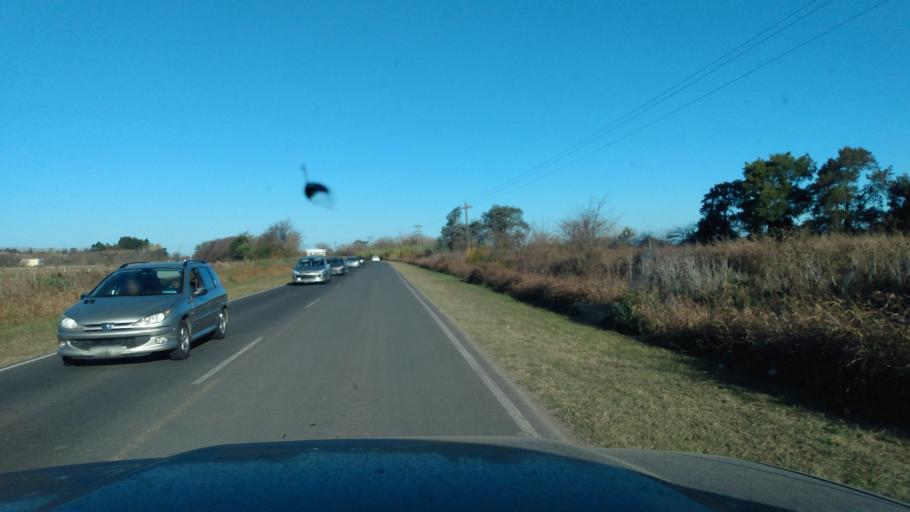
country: AR
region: Buenos Aires
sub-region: Partido de Lujan
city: Lujan
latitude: -34.4929
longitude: -59.2096
